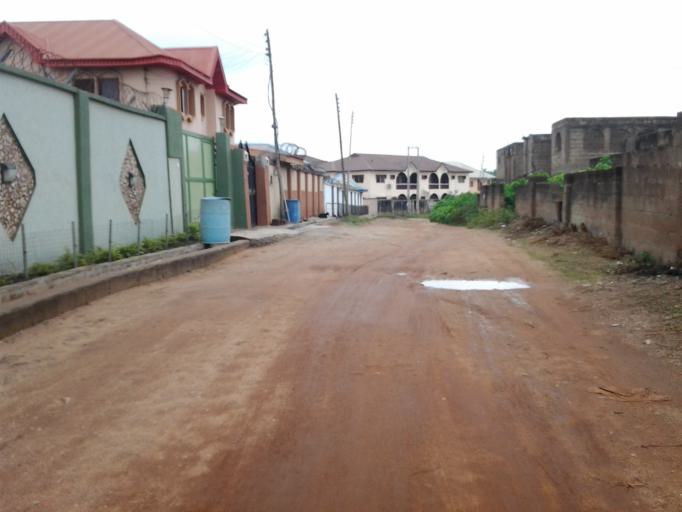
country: NG
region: Oyo
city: Ibadan
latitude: 7.4309
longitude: 3.9560
